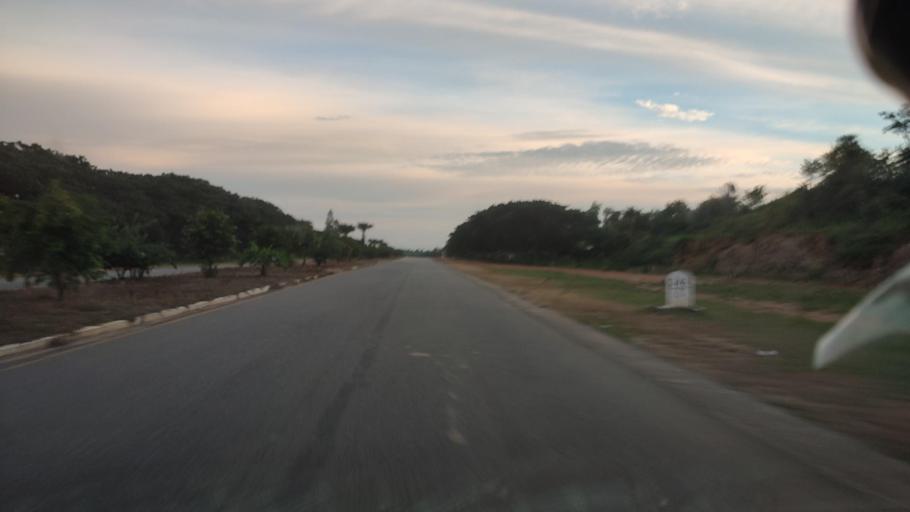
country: MM
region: Mandalay
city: Yamethin
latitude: 20.2720
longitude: 95.8914
